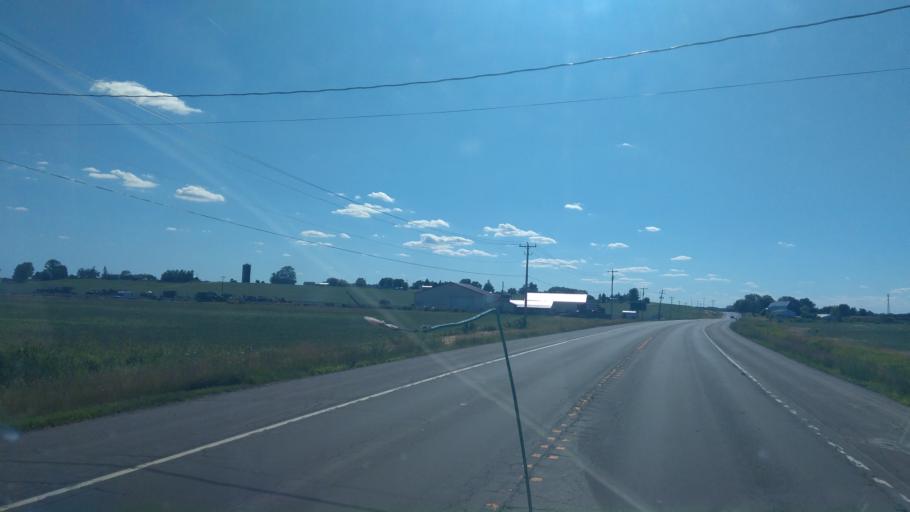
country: US
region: New York
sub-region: Seneca County
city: Waterloo
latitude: 42.9543
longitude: -76.8932
